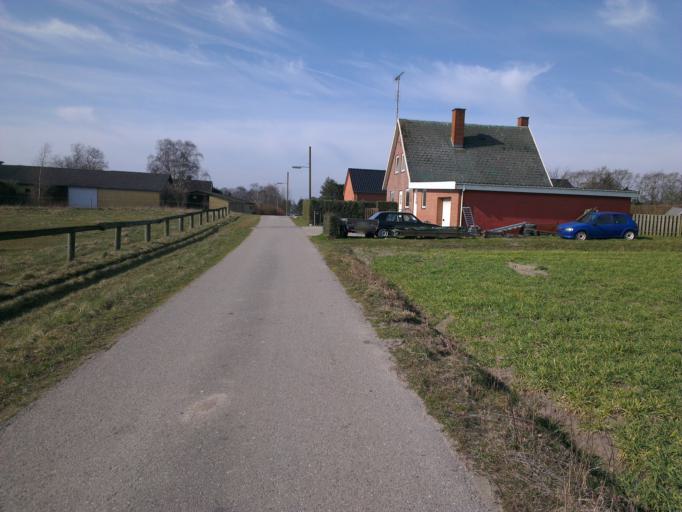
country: DK
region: Capital Region
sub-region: Frederikssund Kommune
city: Jaegerspris
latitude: 55.8052
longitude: 11.9898
